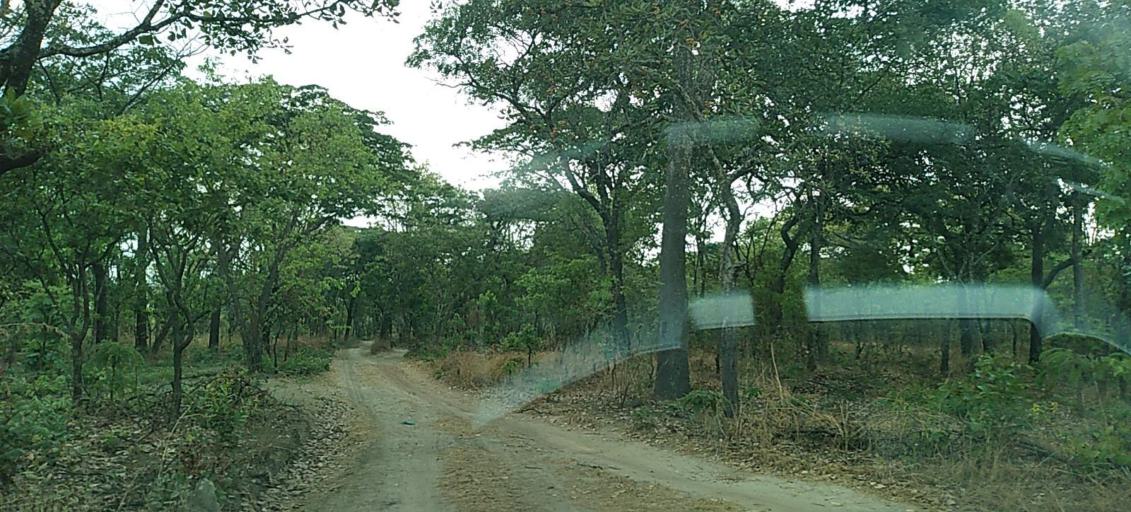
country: ZM
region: North-Western
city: Solwezi
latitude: -12.0974
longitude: 26.2792
